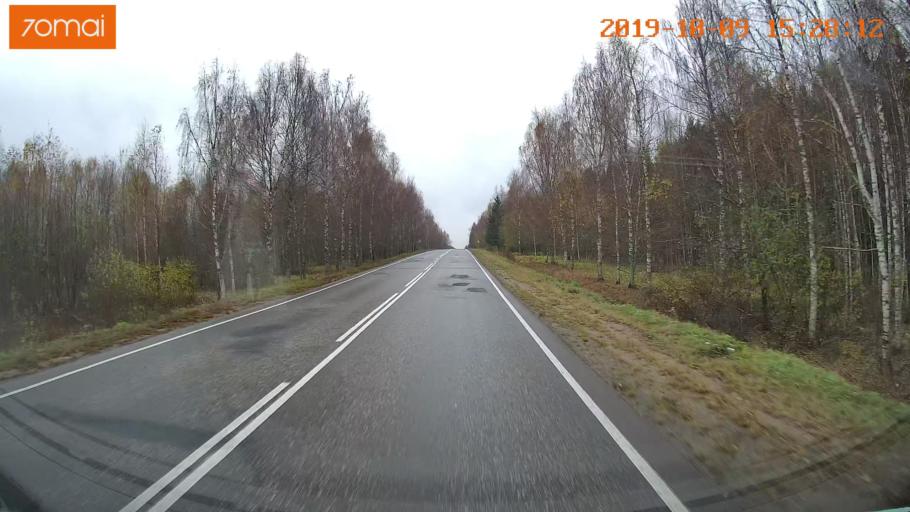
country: RU
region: Kostroma
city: Susanino
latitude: 58.0057
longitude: 41.3639
